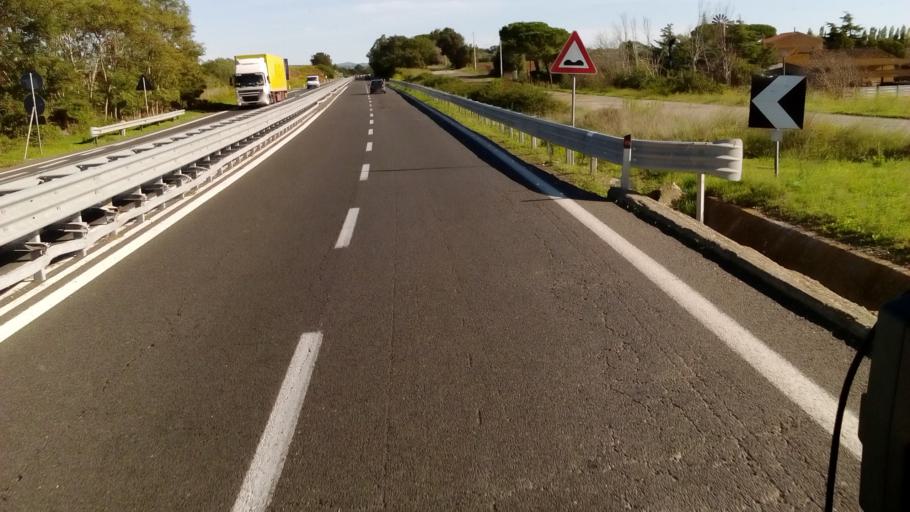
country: IT
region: Latium
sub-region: Provincia di Viterbo
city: Montalto di Castro
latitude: 42.3085
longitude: 11.6561
